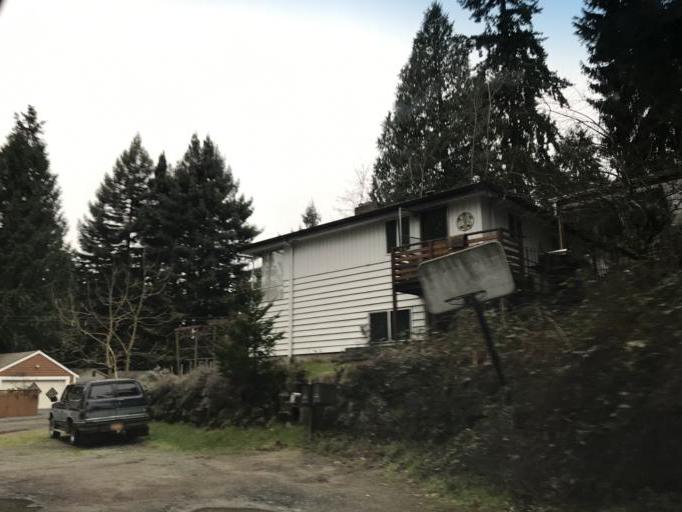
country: US
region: Washington
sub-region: King County
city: Lake Forest Park
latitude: 47.7146
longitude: -122.2931
